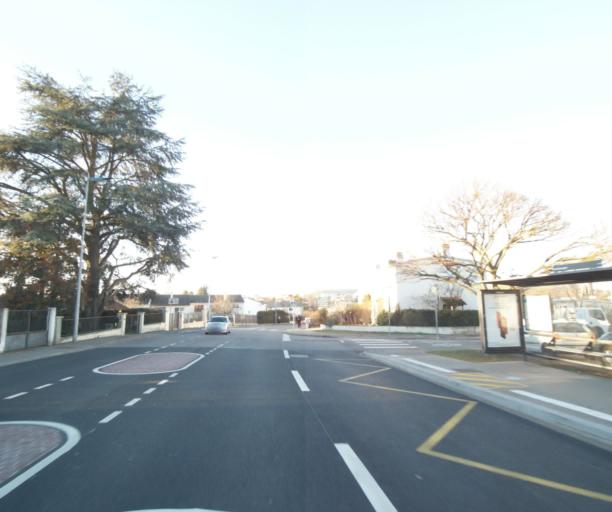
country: FR
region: Lorraine
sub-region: Departement de Meurthe-et-Moselle
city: Tomblaine
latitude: 48.6799
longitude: 6.2166
